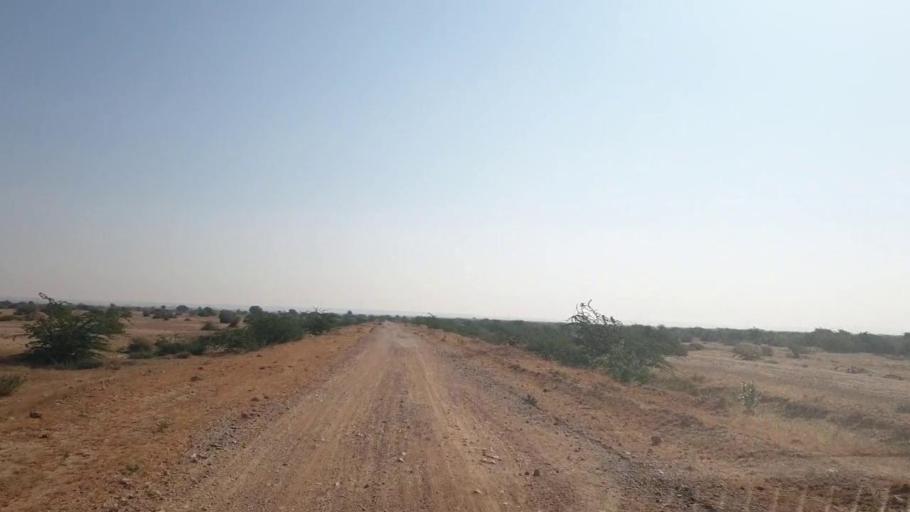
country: PK
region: Sindh
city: Gharo
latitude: 25.1421
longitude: 67.7301
